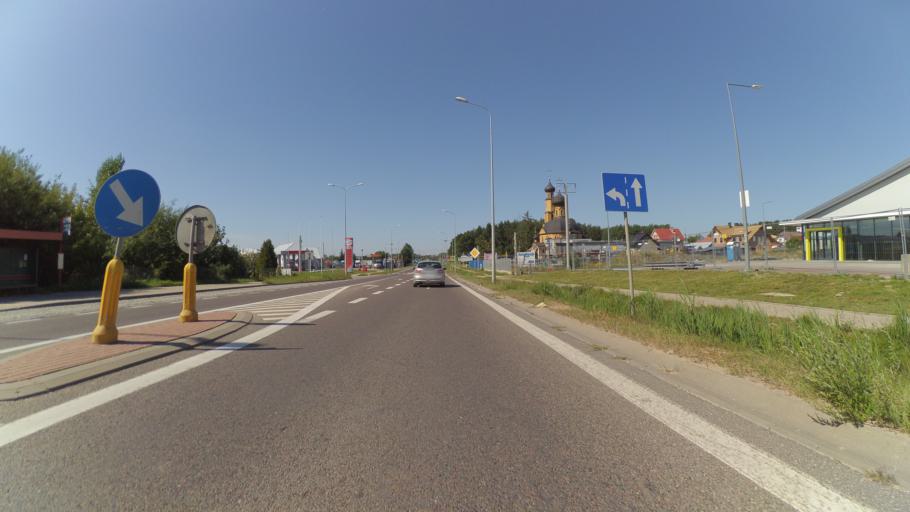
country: PL
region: Podlasie
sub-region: Bialystok
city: Bialystok
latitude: 53.1256
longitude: 23.2421
